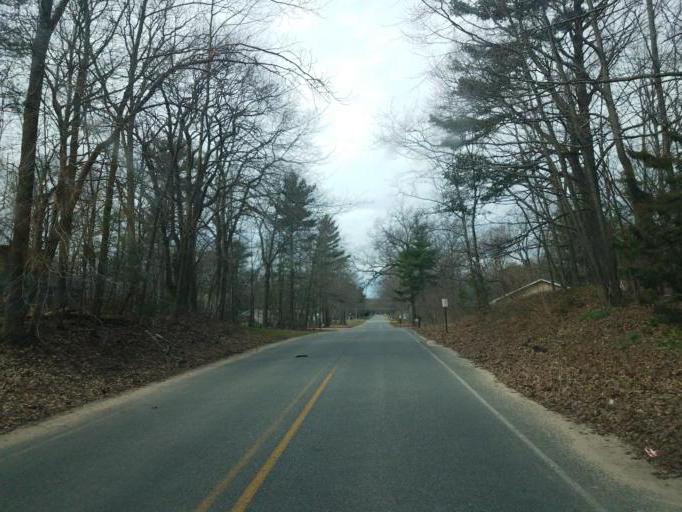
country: US
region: Michigan
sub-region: Oceana County
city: Hart
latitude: 43.6579
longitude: -86.5155
